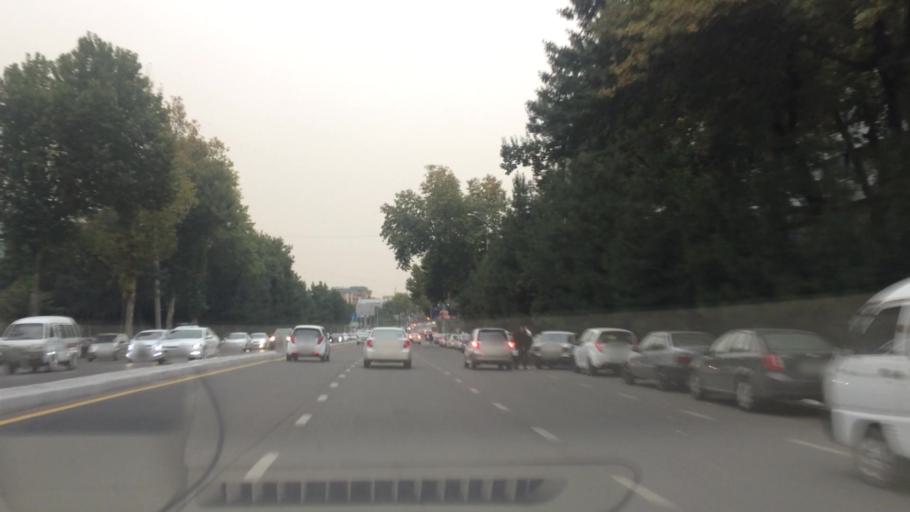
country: UZ
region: Toshkent Shahri
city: Tashkent
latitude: 41.3056
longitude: 69.2826
